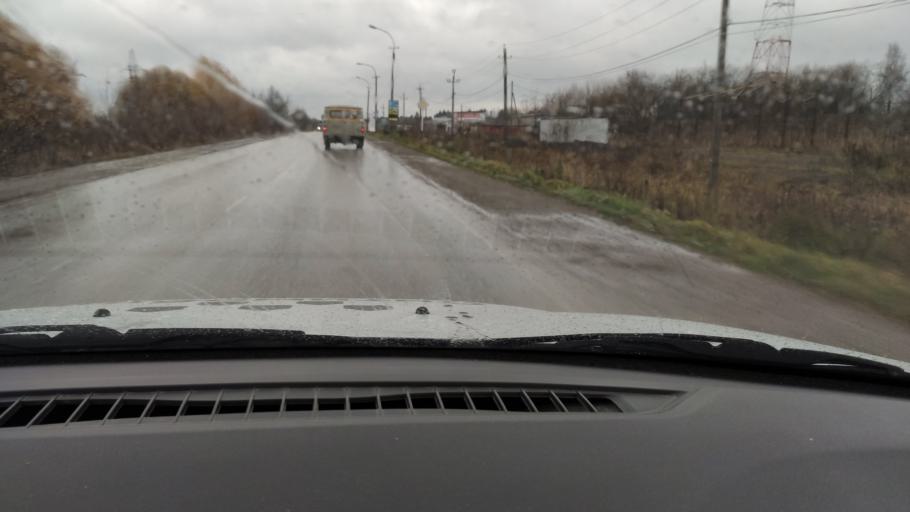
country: RU
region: Perm
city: Sylva
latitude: 58.0266
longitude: 56.7306
